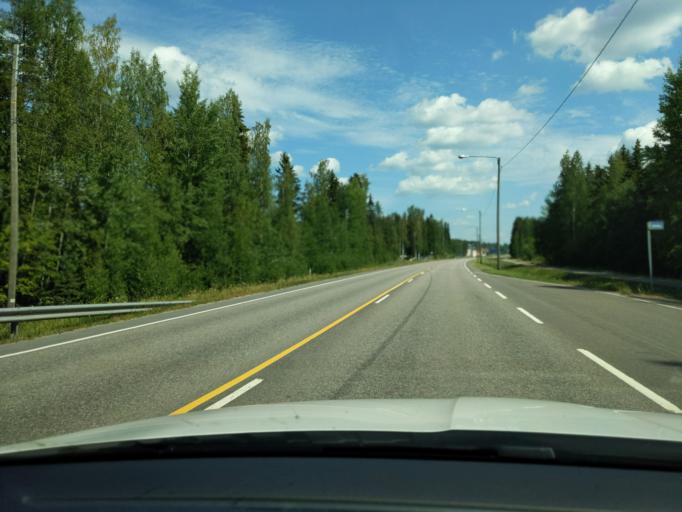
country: FI
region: Uusimaa
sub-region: Helsinki
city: Maentsaelae
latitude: 60.6189
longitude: 25.2793
